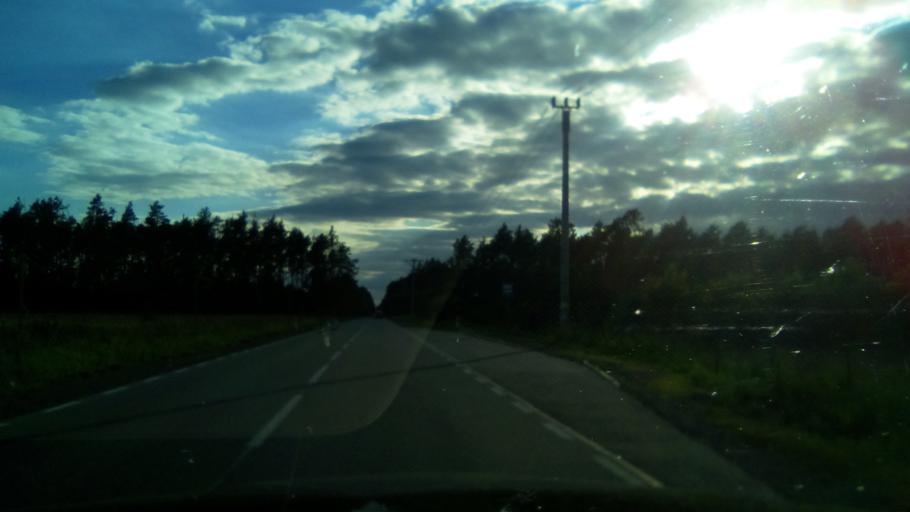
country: PL
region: Masovian Voivodeship
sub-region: Powiat bialobrzeski
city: Bialobrzegi
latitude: 51.6523
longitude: 20.9952
